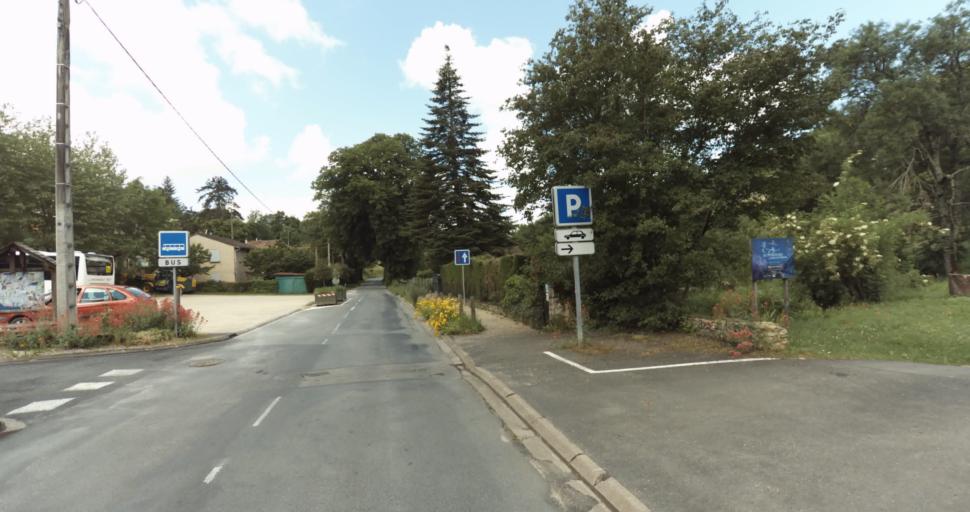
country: FR
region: Aquitaine
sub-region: Departement de la Dordogne
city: Beaumont-du-Perigord
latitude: 44.8119
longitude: 0.8706
